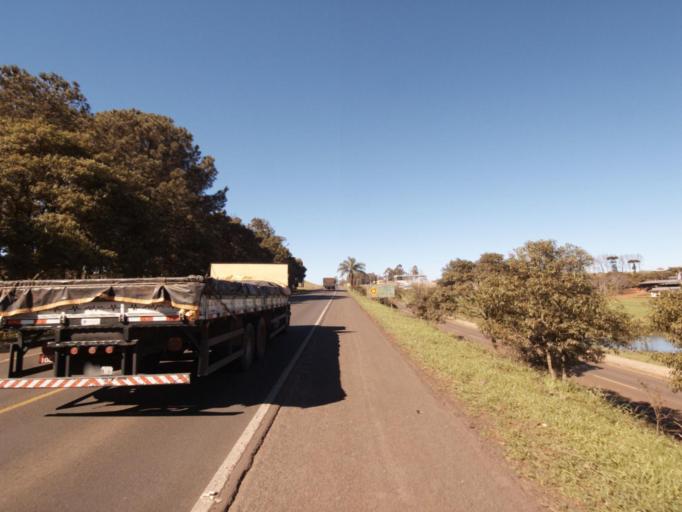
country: BR
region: Santa Catarina
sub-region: Chapeco
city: Chapeco
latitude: -26.8314
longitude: -52.9951
